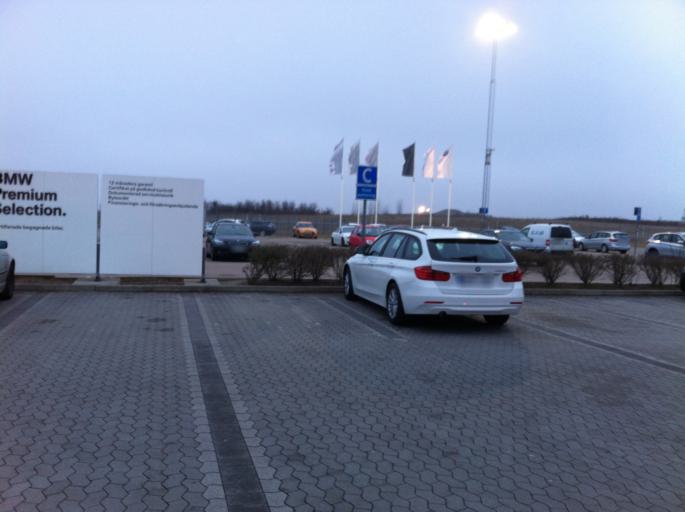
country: SE
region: Skane
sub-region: Malmo
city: Oxie
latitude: 55.5594
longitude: 13.0729
